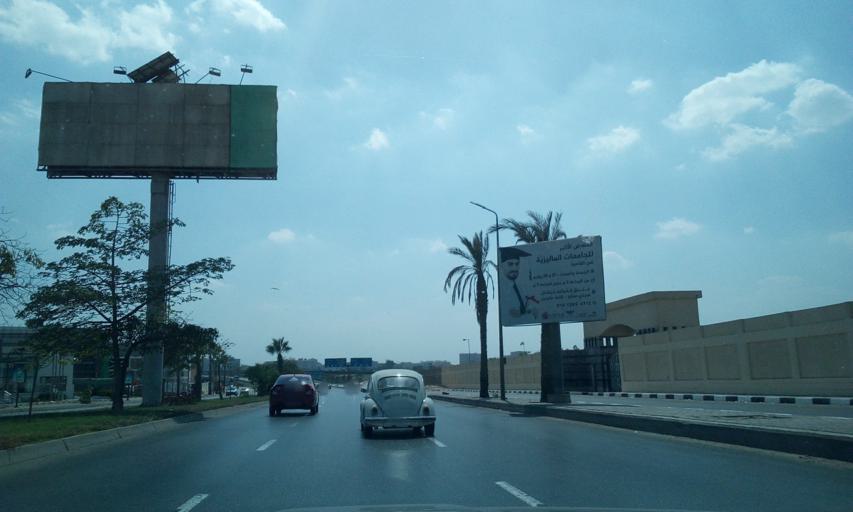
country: EG
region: Muhafazat al Qahirah
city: Cairo
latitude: 30.0843
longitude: 31.3645
